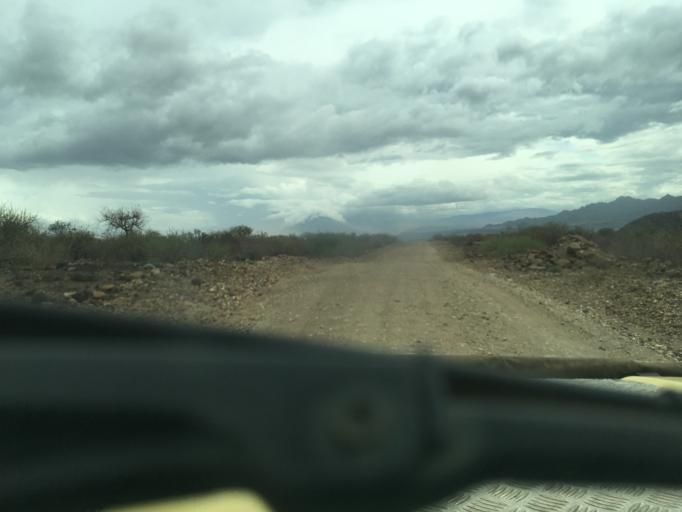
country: KE
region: Kajiado
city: Magadi
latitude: -2.4637
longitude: 35.8761
